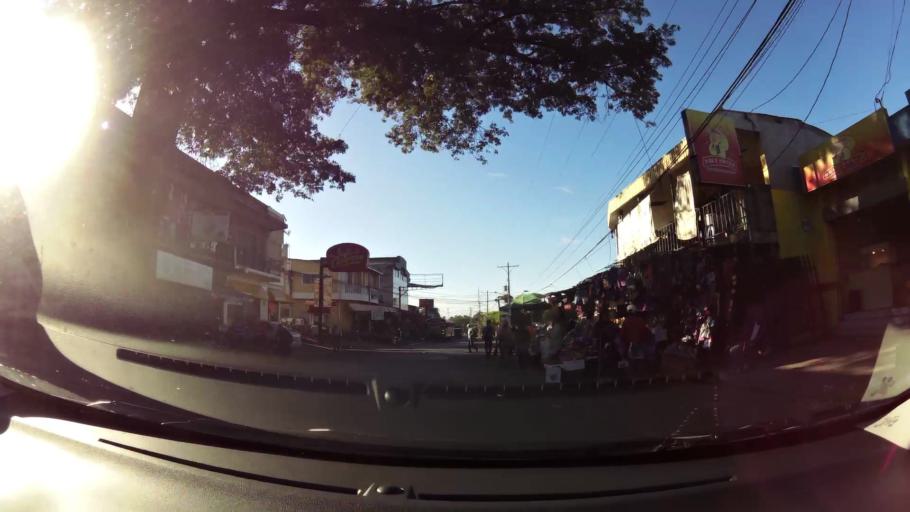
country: SV
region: Sonsonate
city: Sonsonate
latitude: 13.7119
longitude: -89.7175
